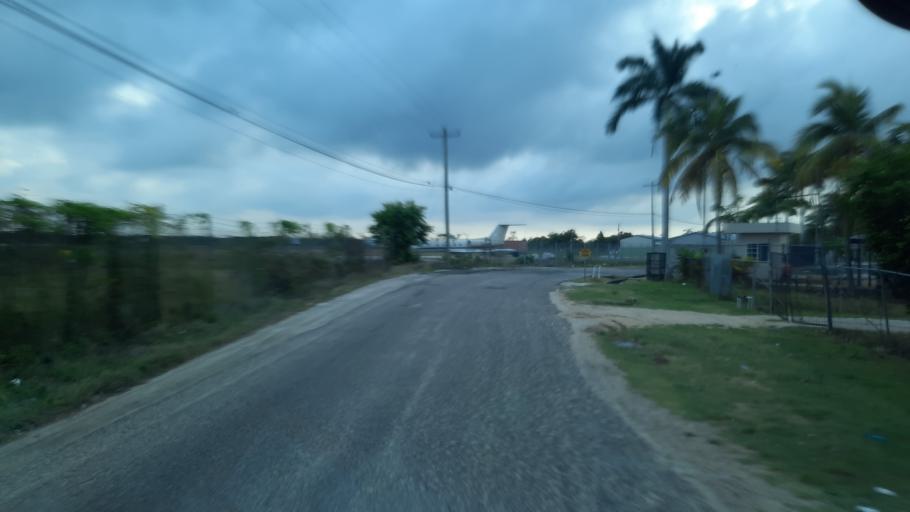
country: BZ
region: Belize
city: Belize City
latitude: 17.5430
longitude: -88.2994
